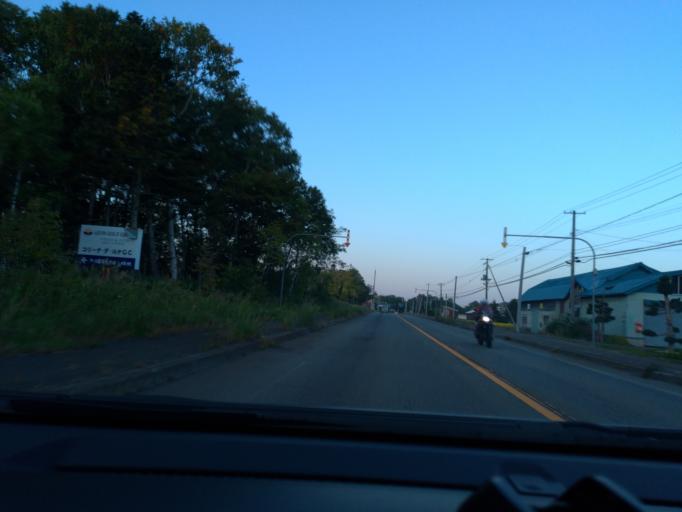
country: JP
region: Hokkaido
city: Tobetsu
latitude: 43.3230
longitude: 141.6154
